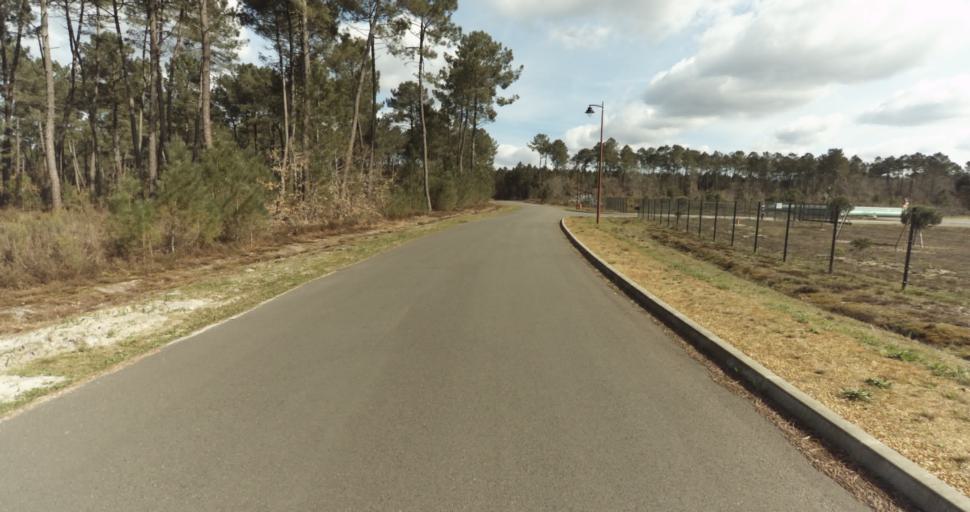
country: FR
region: Aquitaine
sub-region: Departement des Landes
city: Roquefort
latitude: 44.0570
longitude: -0.3150
